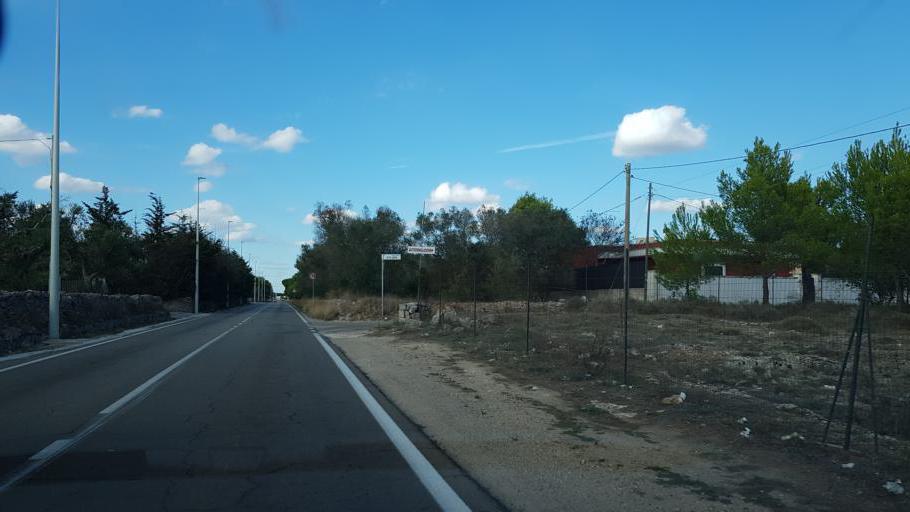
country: IT
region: Apulia
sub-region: Provincia di Lecce
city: Nardo
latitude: 40.1403
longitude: 18.0189
